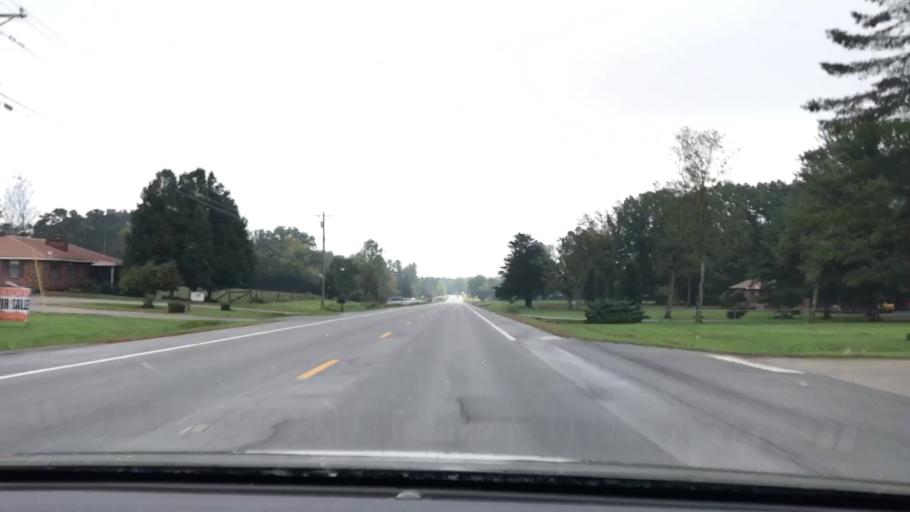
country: US
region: Tennessee
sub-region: Fentress County
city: Grimsley
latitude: 36.2481
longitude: -84.9982
